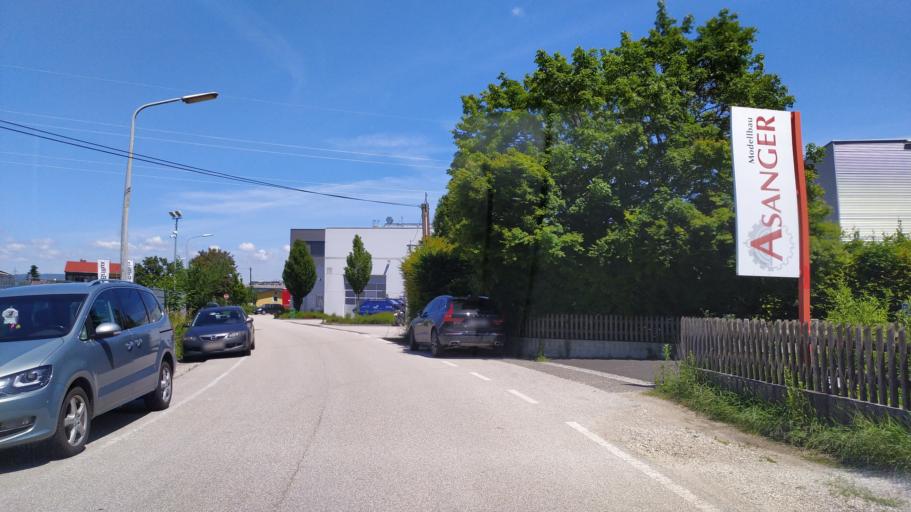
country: AT
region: Upper Austria
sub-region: Politischer Bezirk Linz-Land
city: Ansfelden
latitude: 48.2352
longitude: 14.2766
